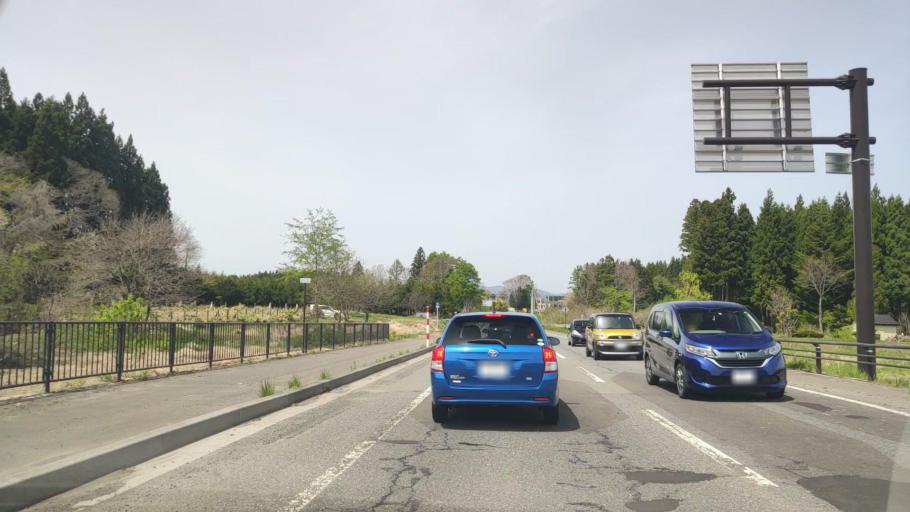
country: JP
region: Aomori
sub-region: Misawa Shi
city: Inuotose
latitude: 40.7108
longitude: 141.1593
